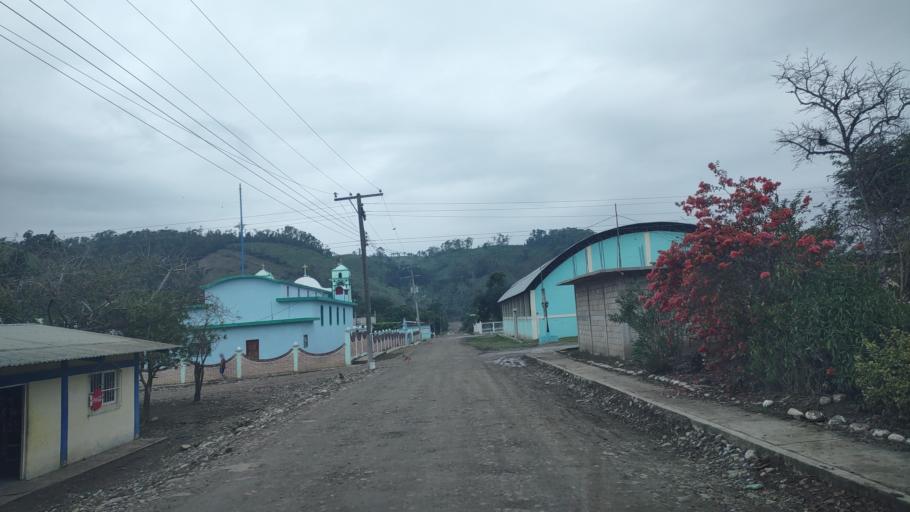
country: MX
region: Veracruz
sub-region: Coatzintla
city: Manuel Maria Contreras
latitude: 20.3998
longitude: -97.4396
